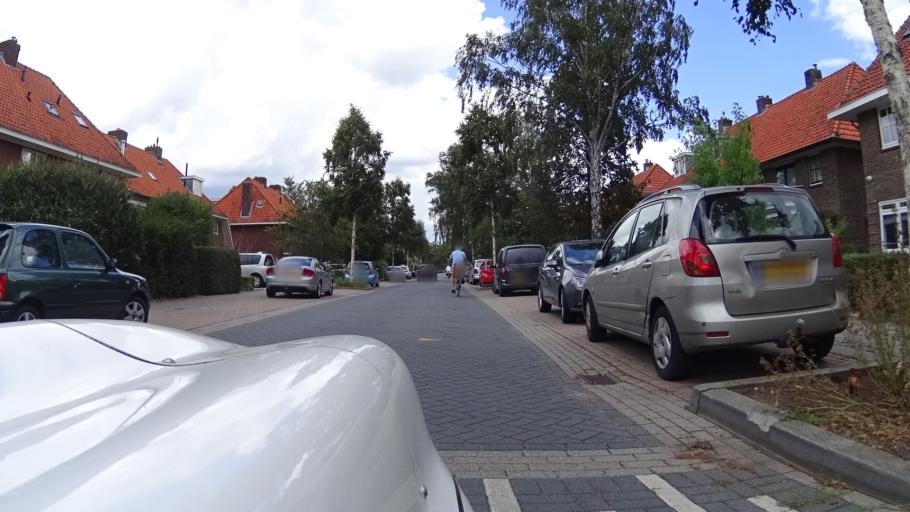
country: NL
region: Utrecht
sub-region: Gemeente De Bilt
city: De Bilt
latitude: 52.1130
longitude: 5.1796
